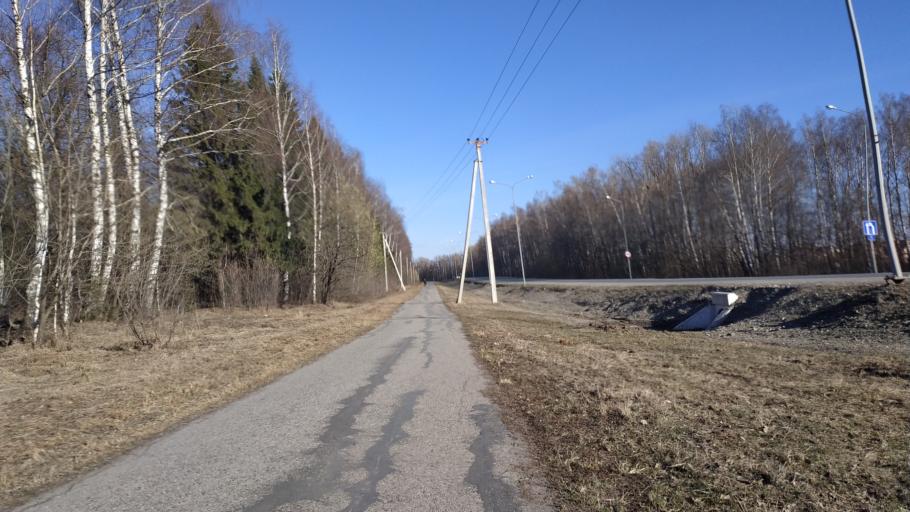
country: RU
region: Chuvashia
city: Novyye Lapsary
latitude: 56.1314
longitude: 47.1129
